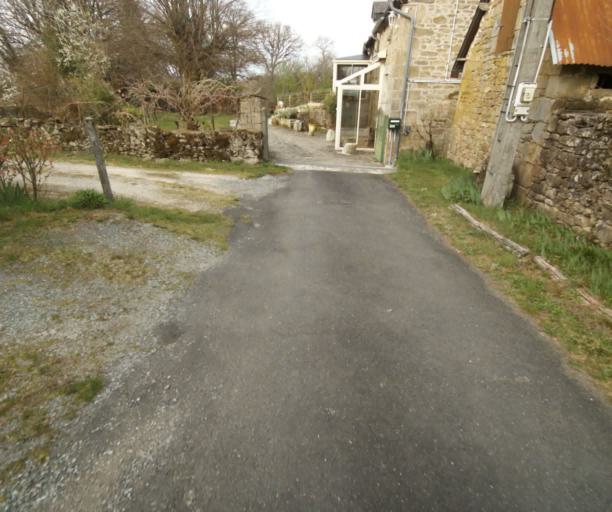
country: FR
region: Limousin
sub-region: Departement de la Correze
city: Treignac
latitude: 45.4449
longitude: 1.8120
